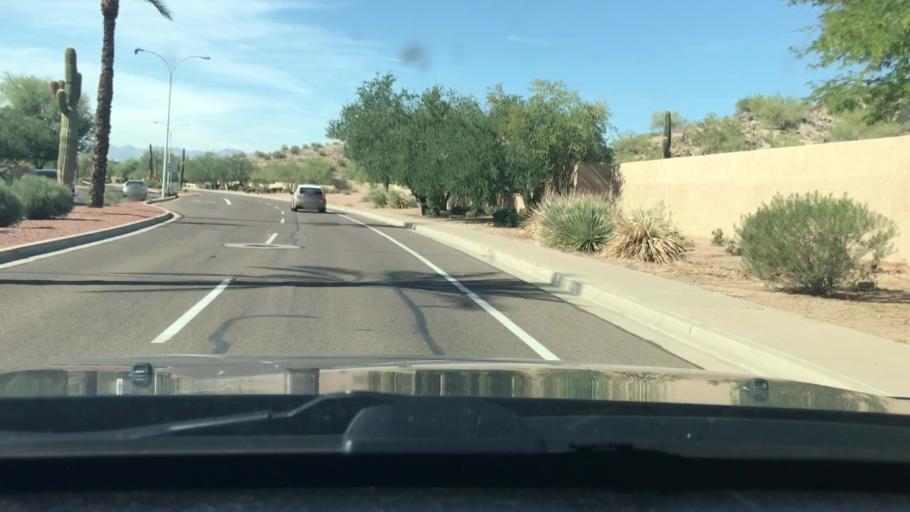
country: US
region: Arizona
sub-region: Maricopa County
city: Guadalupe
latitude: 33.3156
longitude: -112.0139
